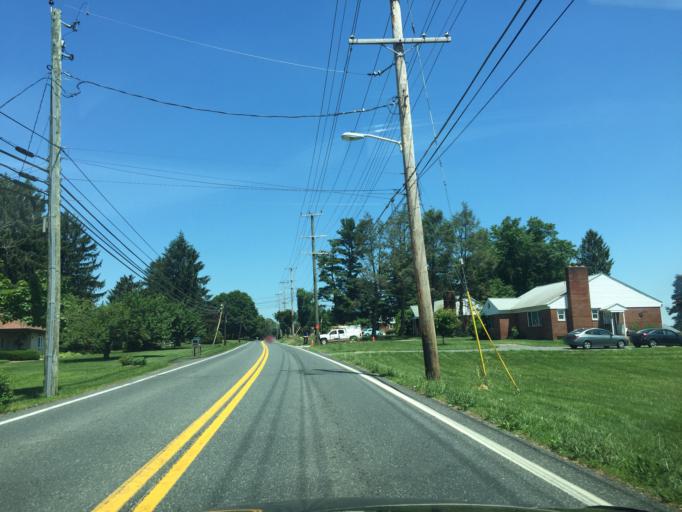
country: US
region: Maryland
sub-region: Harford County
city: Jarrettsville
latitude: 39.5983
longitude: -76.4763
